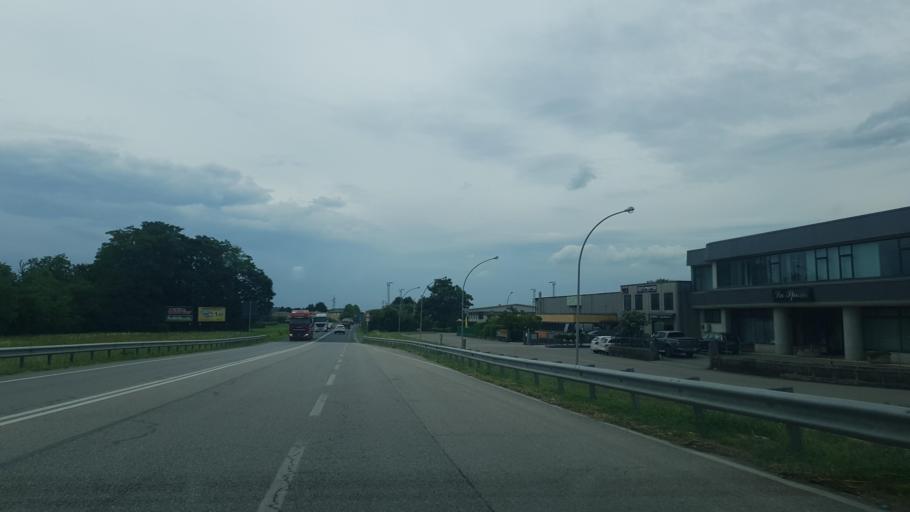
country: IT
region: Veneto
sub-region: Provincia di Treviso
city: Cornuda
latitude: 45.8378
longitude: 12.0151
